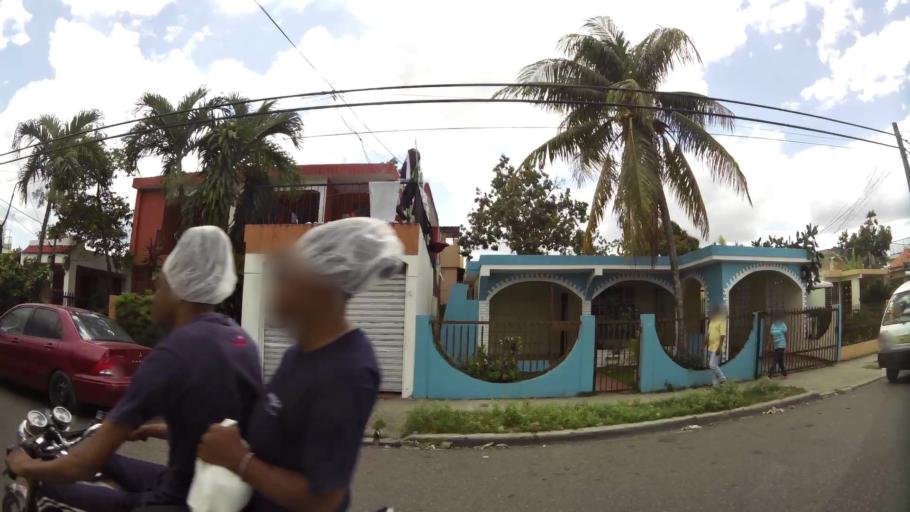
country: DO
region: Nacional
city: Ensanche Luperon
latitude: 18.5292
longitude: -69.9047
